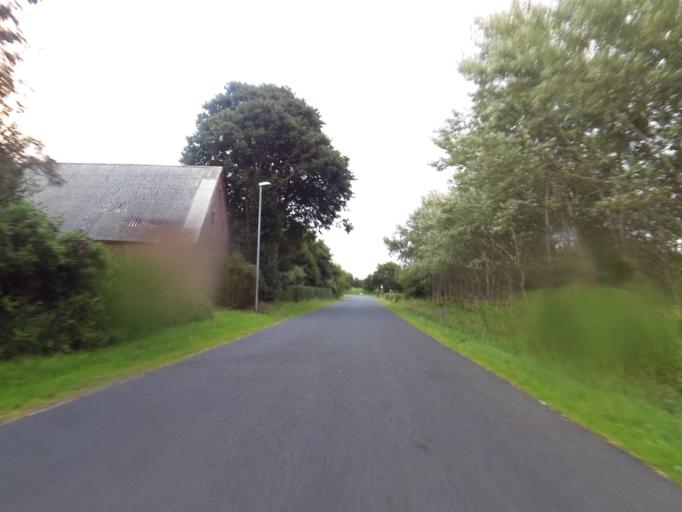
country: DK
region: South Denmark
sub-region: Esbjerg Kommune
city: Ribe
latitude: 55.2789
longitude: 8.8285
